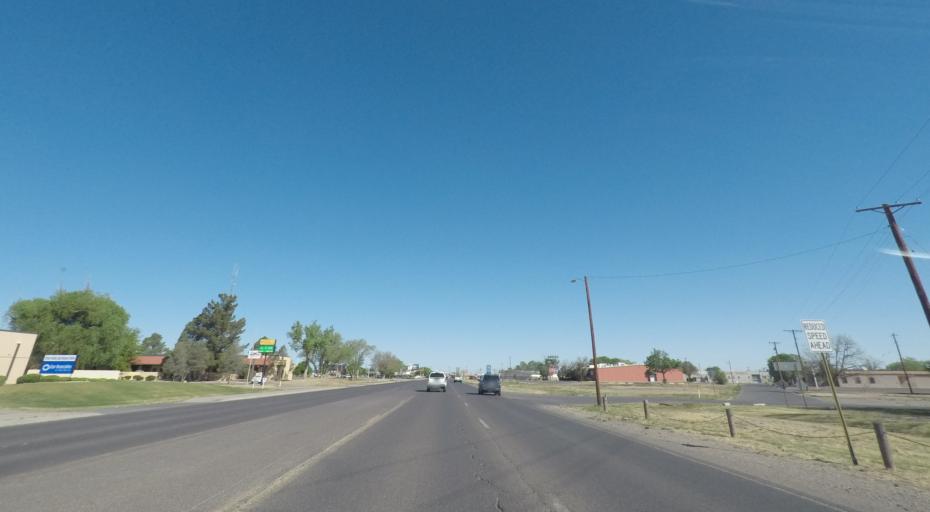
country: US
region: New Mexico
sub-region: Chaves County
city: Roswell
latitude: 33.3739
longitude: -104.5188
